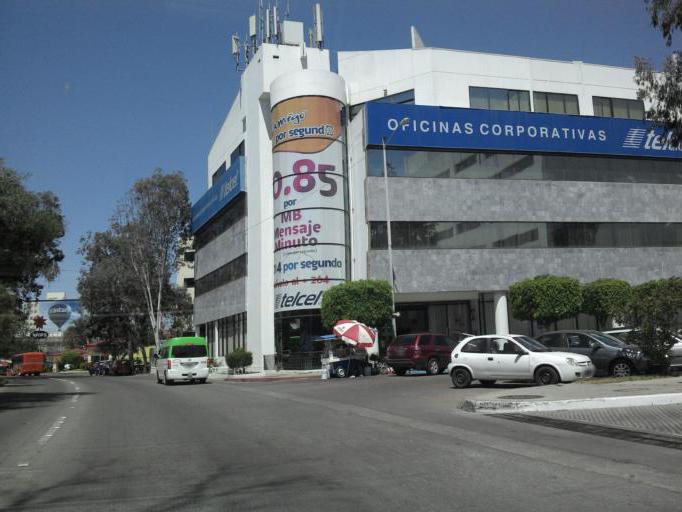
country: MX
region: Baja California
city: Tijuana
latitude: 32.5176
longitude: -117.0086
